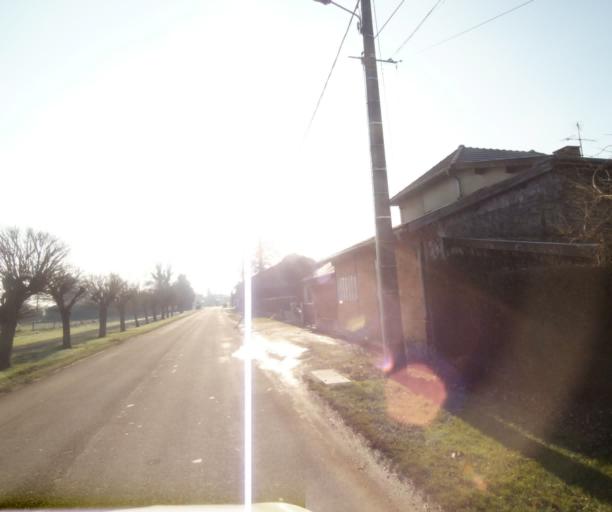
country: FR
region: Champagne-Ardenne
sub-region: Departement de la Haute-Marne
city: Montier-en-Der
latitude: 48.4747
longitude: 4.7635
